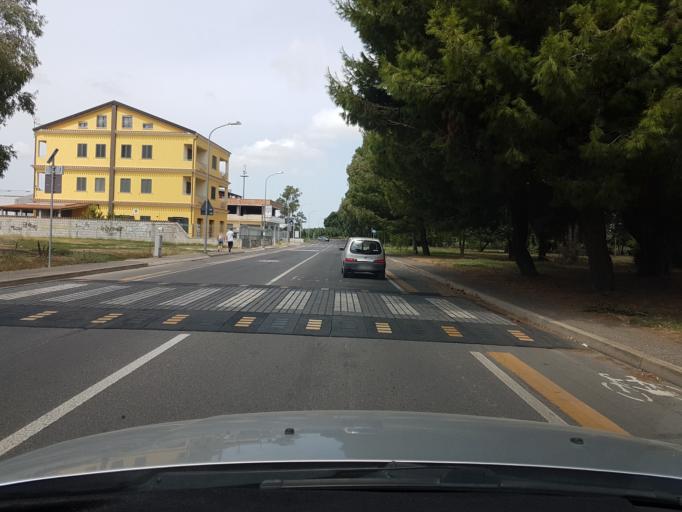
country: IT
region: Sardinia
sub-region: Provincia di Oristano
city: Oristano
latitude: 39.9139
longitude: 8.5893
